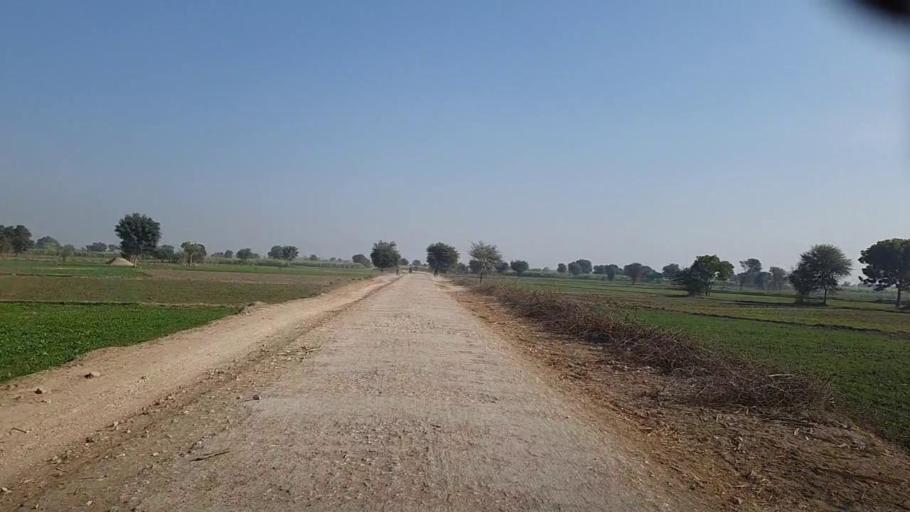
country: PK
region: Sindh
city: Darya Khan Marri
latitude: 26.6713
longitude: 68.3264
